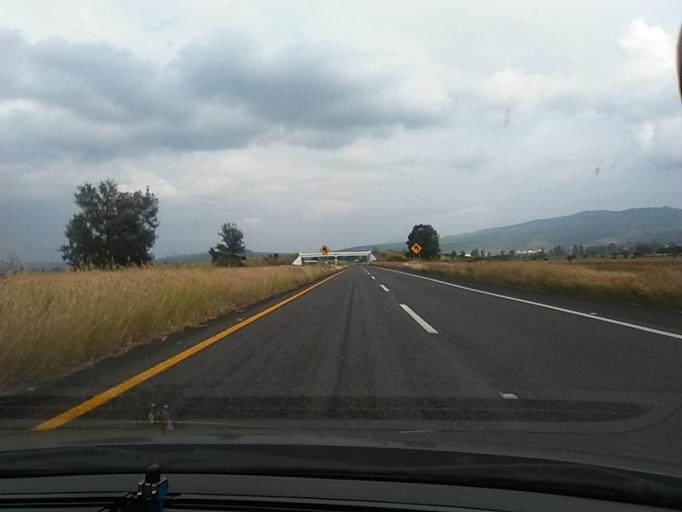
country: MX
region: Michoacan
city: Ecuandureo
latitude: 20.1753
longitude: -102.2360
